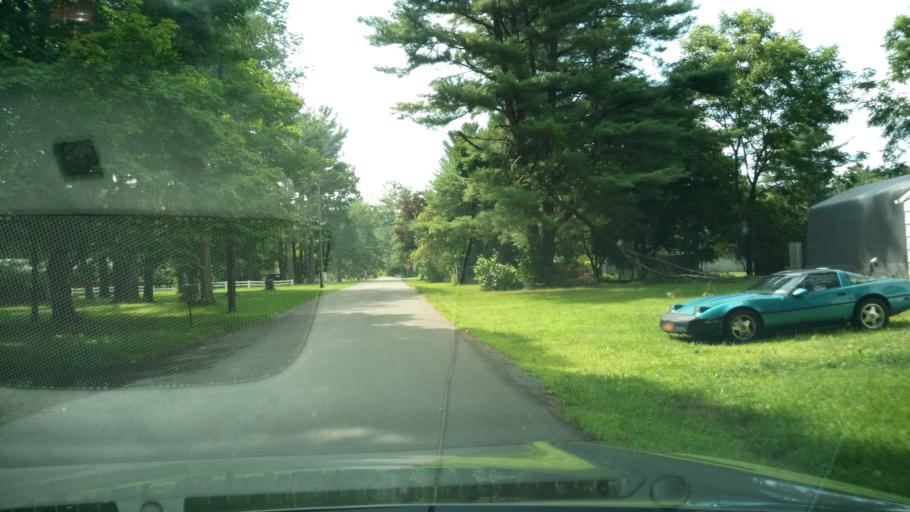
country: US
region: New York
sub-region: Chemung County
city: West Elmira
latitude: 42.0843
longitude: -76.8733
